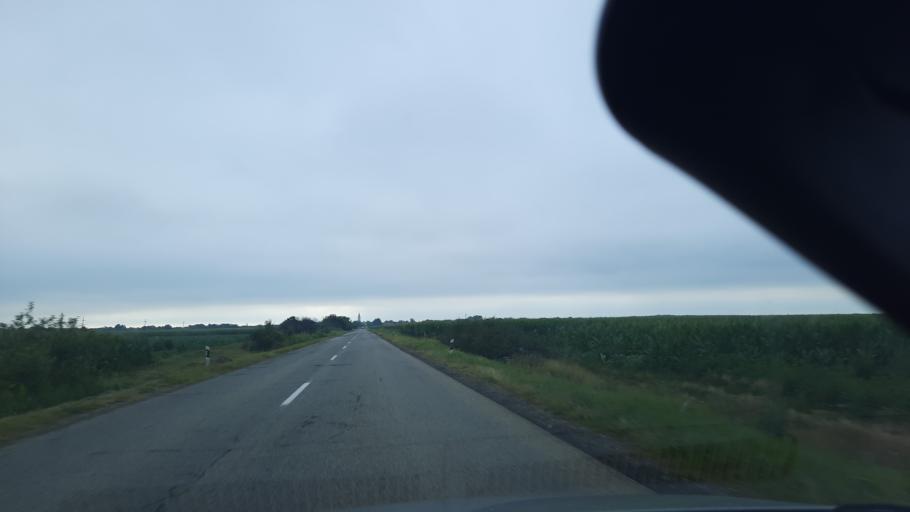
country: RS
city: Farkazdin
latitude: 45.1941
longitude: 20.4572
